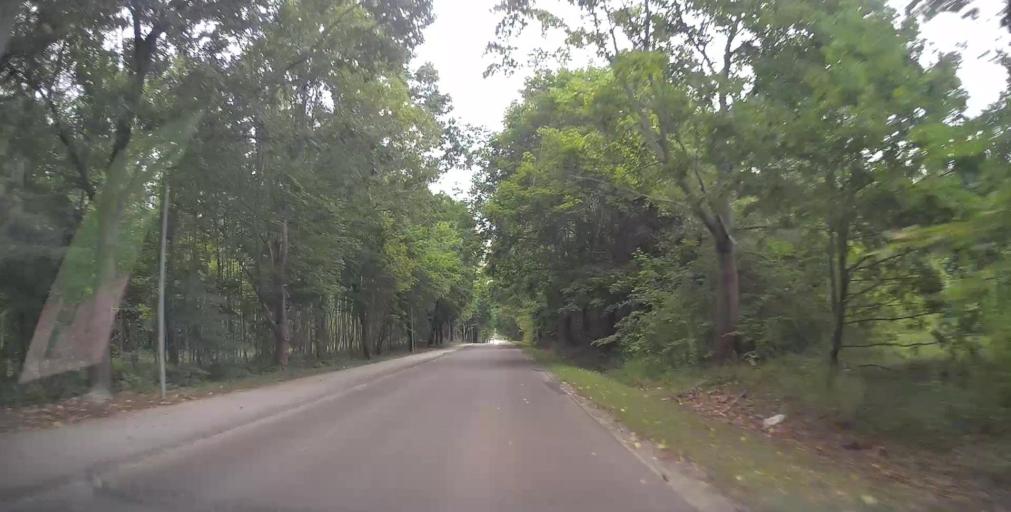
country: PL
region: Masovian Voivodeship
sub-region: Powiat bialobrzeski
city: Bialobrzegi
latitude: 51.6355
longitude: 20.9535
